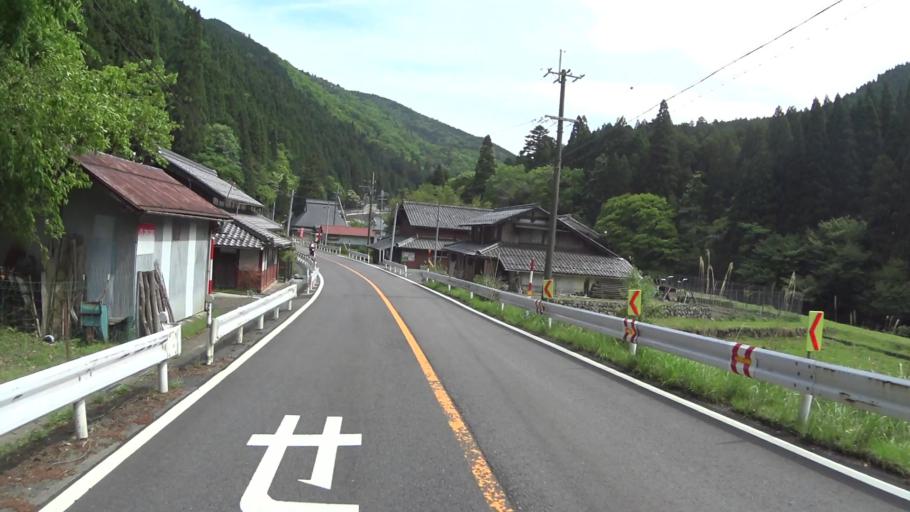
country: JP
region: Shiga Prefecture
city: Kitahama
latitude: 35.1999
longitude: 135.8599
